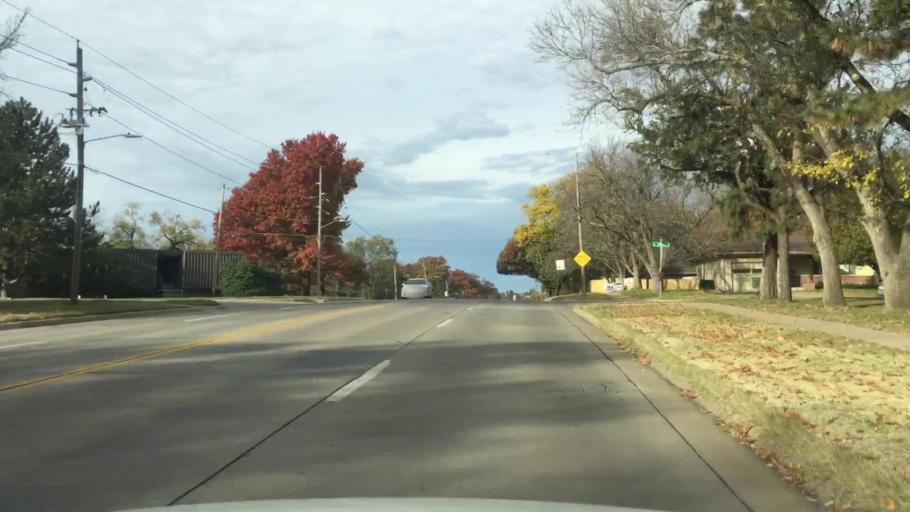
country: US
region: Kansas
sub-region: Shawnee County
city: Topeka
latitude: 39.0153
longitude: -95.7030
